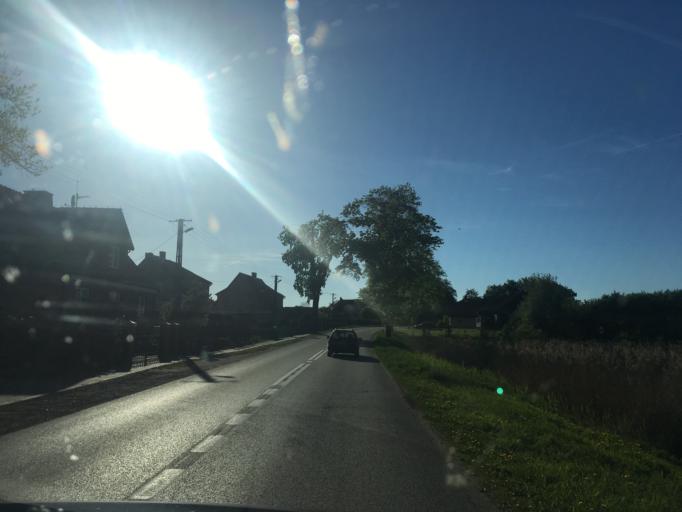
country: PL
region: Warmian-Masurian Voivodeship
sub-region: Powiat piski
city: Ruciane-Nida
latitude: 53.6880
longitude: 21.4912
